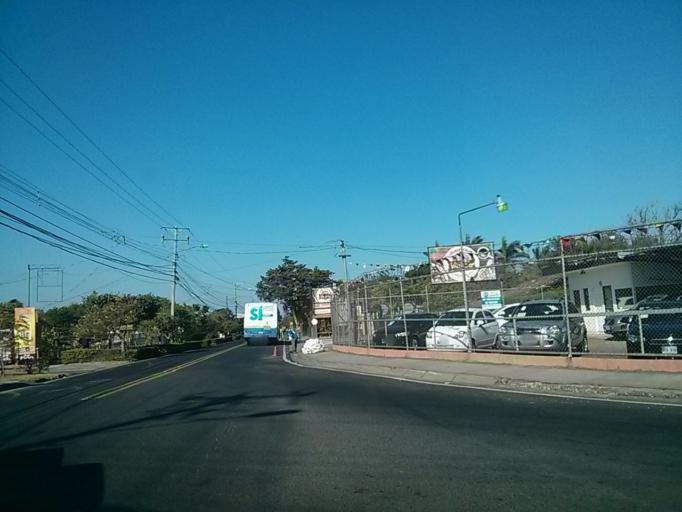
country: CR
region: Heredia
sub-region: Canton de Belen
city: San Antonio
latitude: 9.9824
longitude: -84.1905
